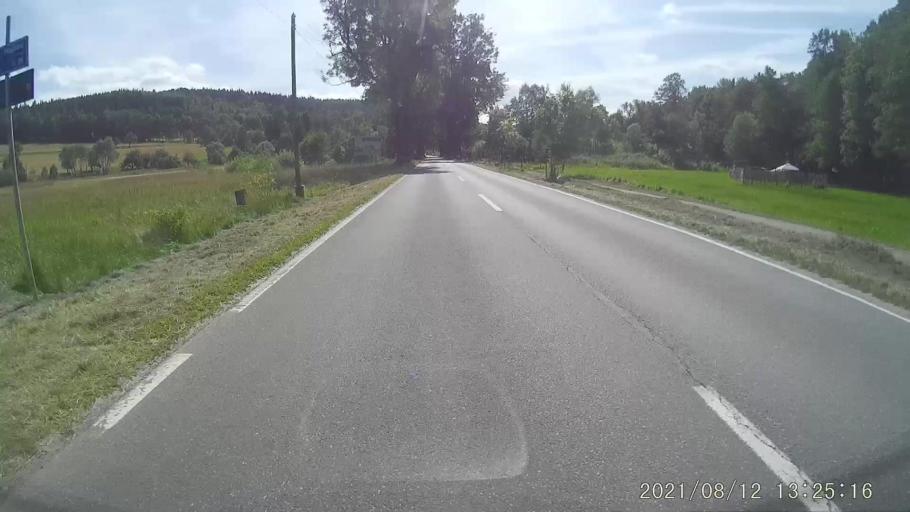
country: PL
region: Lower Silesian Voivodeship
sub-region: Powiat klodzki
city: Ladek-Zdroj
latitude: 50.3199
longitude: 16.8875
